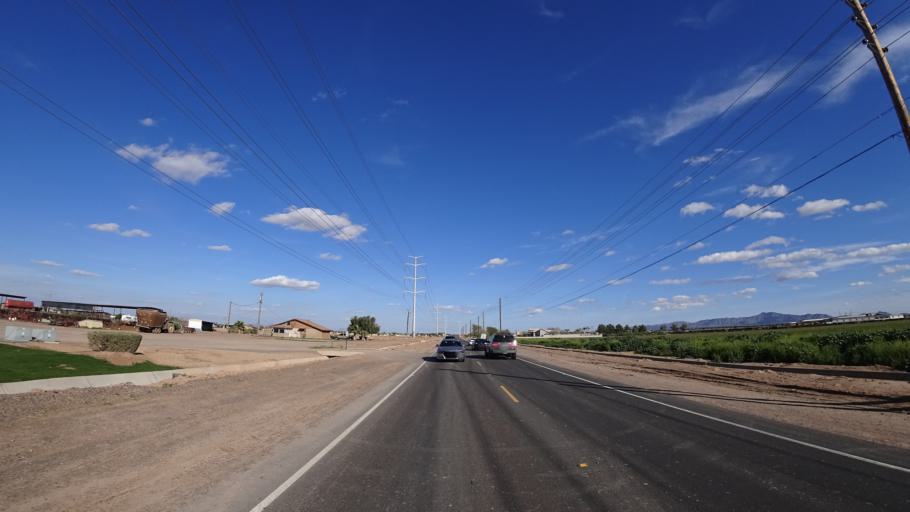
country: US
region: Arizona
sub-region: Maricopa County
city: Tolleson
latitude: 33.4078
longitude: -112.2435
